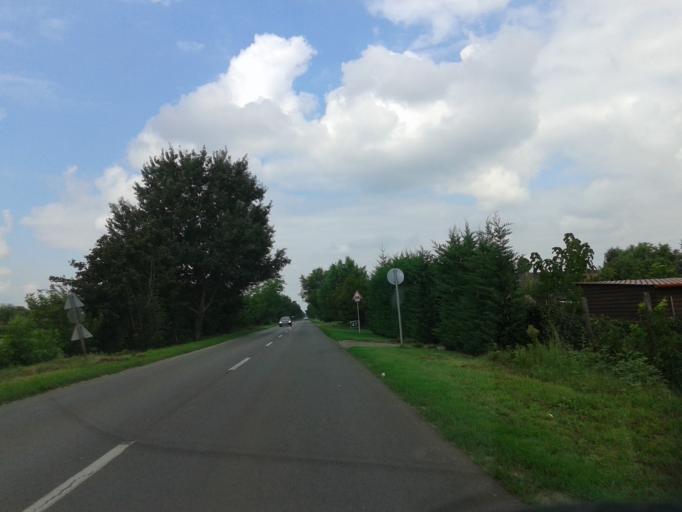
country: HU
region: Csongrad
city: Domaszek
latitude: 46.2752
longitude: 20.0222
